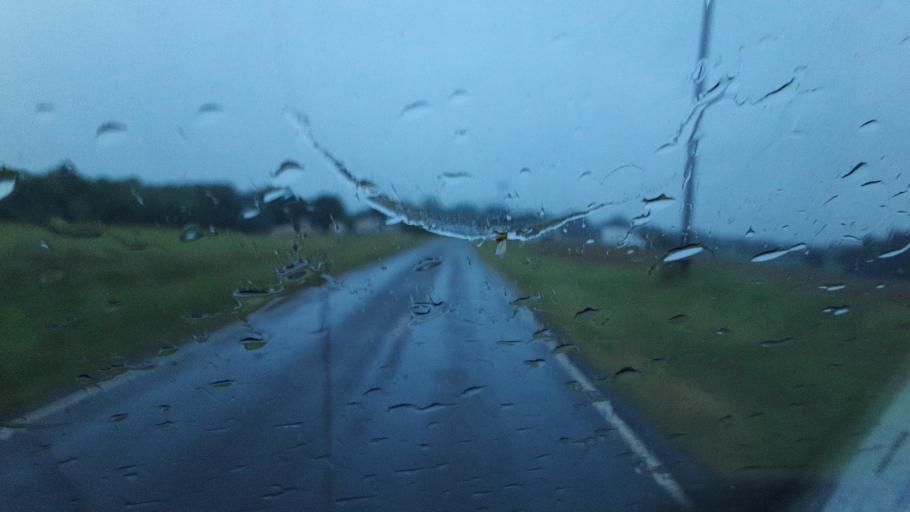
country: US
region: North Carolina
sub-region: Yadkin County
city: Jonesville
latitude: 36.0768
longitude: -80.8530
